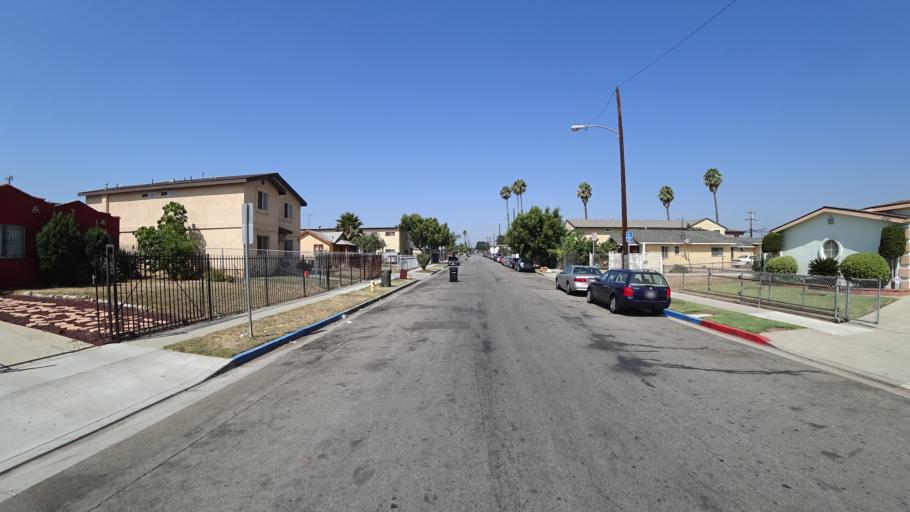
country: US
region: California
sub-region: Los Angeles County
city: Westmont
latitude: 33.9401
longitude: -118.2934
